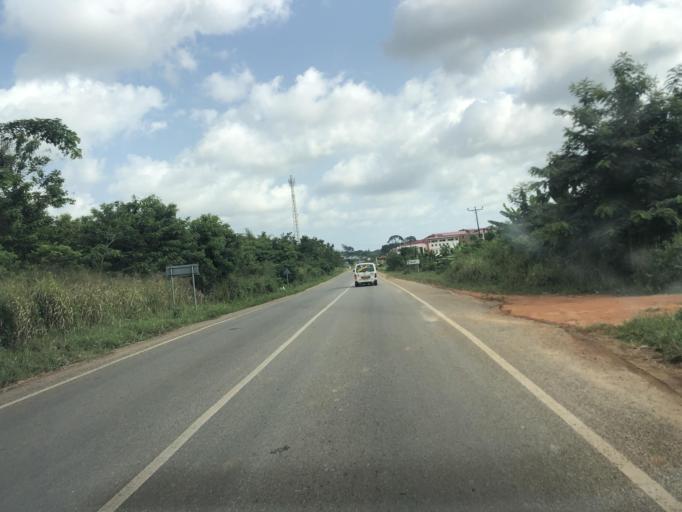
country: GH
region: Central
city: Cape Coast
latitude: 5.1891
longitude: -1.3131
